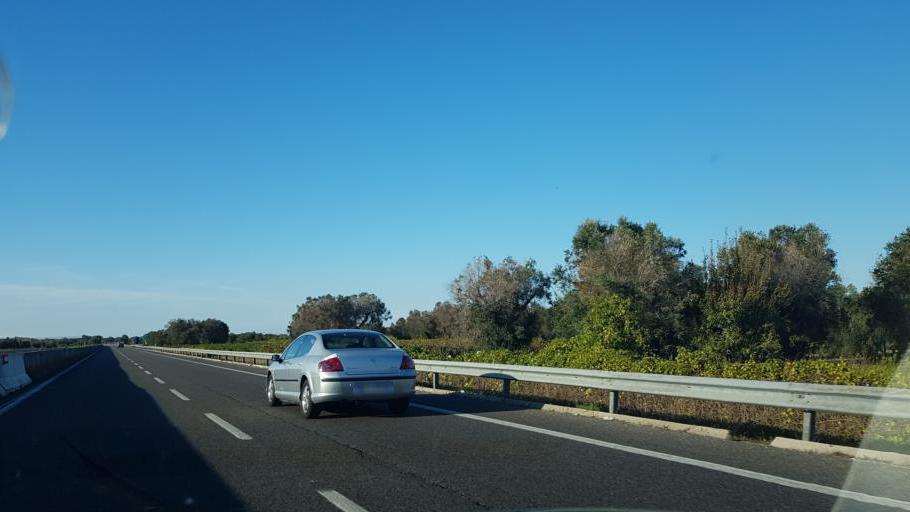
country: IT
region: Apulia
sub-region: Provincia di Brindisi
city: San Pietro Vernotico
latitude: 40.5280
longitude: 18.0123
